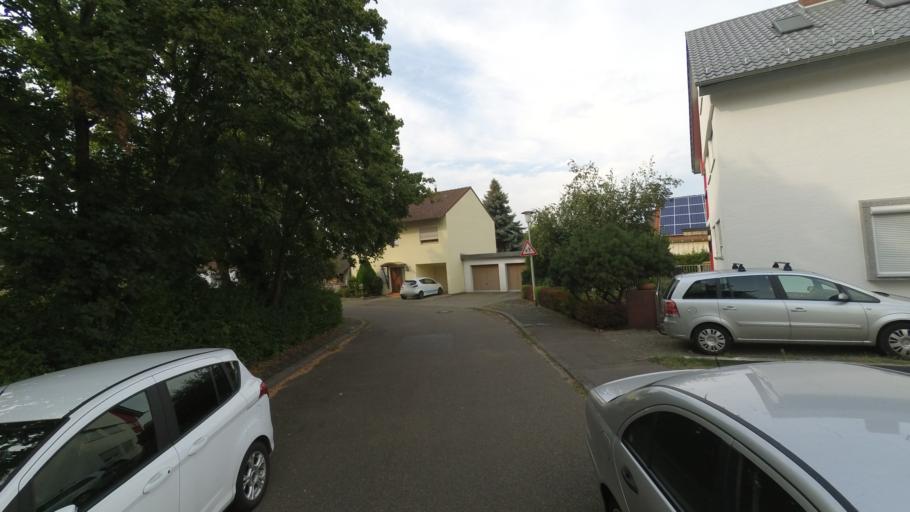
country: DE
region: Rheinland-Pfalz
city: Altrip
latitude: 49.4445
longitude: 8.5178
